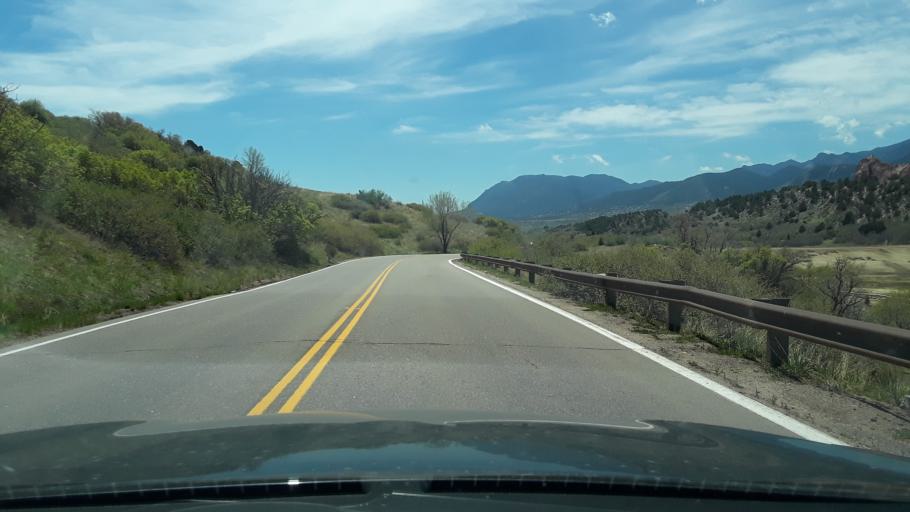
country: US
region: Colorado
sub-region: El Paso County
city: Manitou Springs
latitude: 38.8856
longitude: -104.8741
